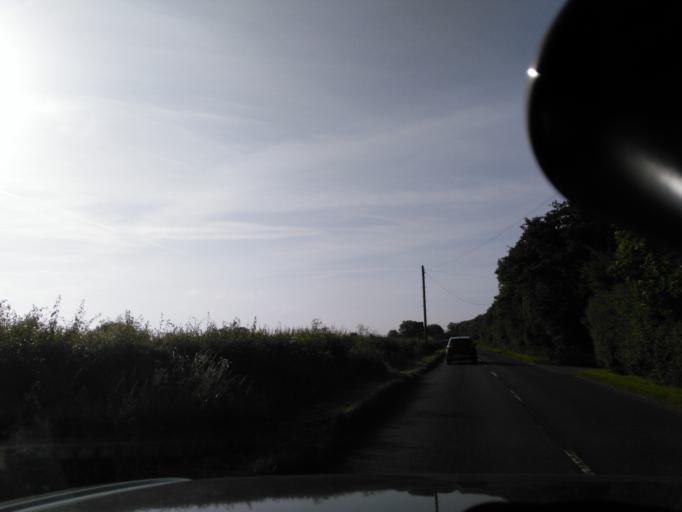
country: GB
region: England
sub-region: Wiltshire
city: Marston
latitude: 51.3254
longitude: -2.0620
